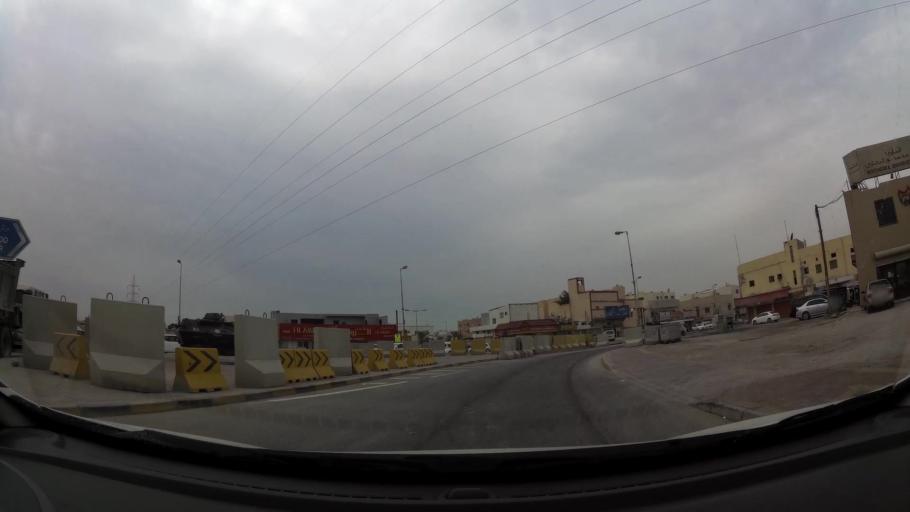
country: BH
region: Northern
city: Sitrah
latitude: 26.1320
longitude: 50.6011
